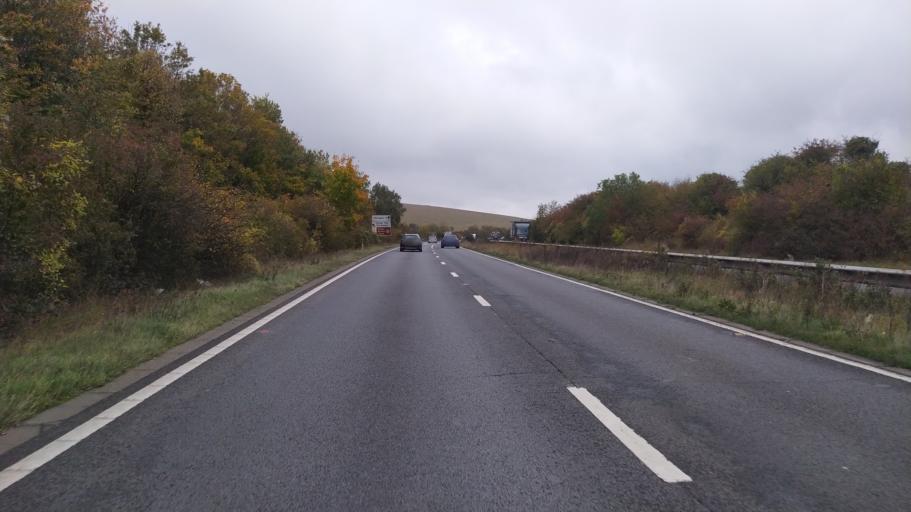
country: GB
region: England
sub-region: Hampshire
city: Cowplain
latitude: 50.9495
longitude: -0.9818
